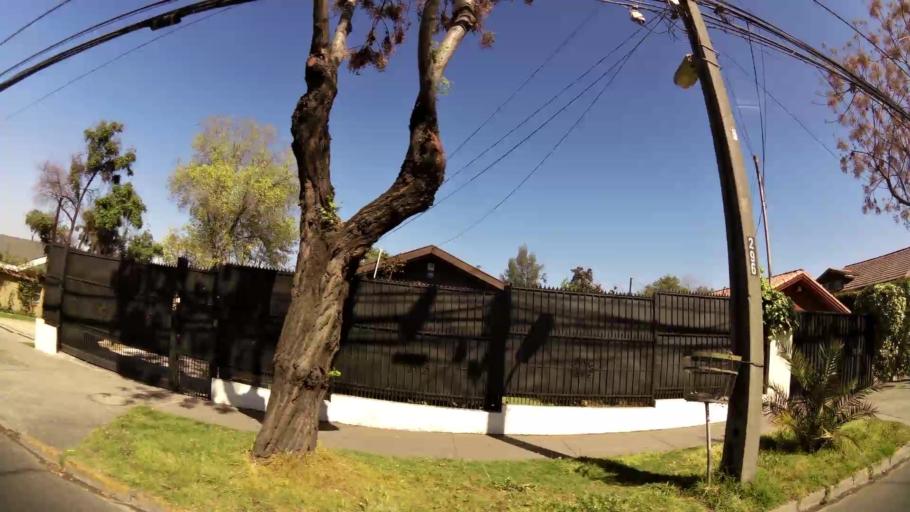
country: CL
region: Santiago Metropolitan
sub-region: Provincia de Santiago
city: Villa Presidente Frei, Nunoa, Santiago, Chile
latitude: -33.4087
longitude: -70.5369
